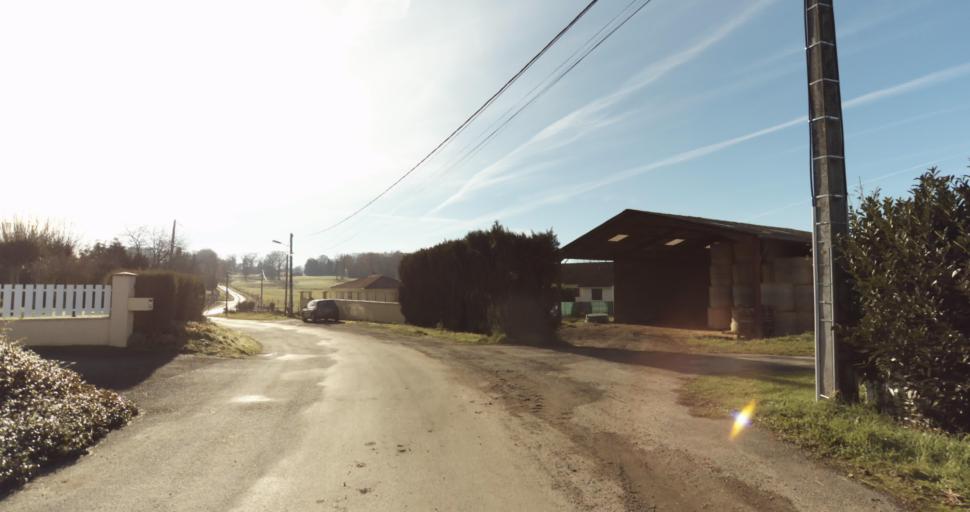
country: FR
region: Limousin
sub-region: Departement de la Haute-Vienne
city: Sereilhac
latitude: 45.7873
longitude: 1.0934
